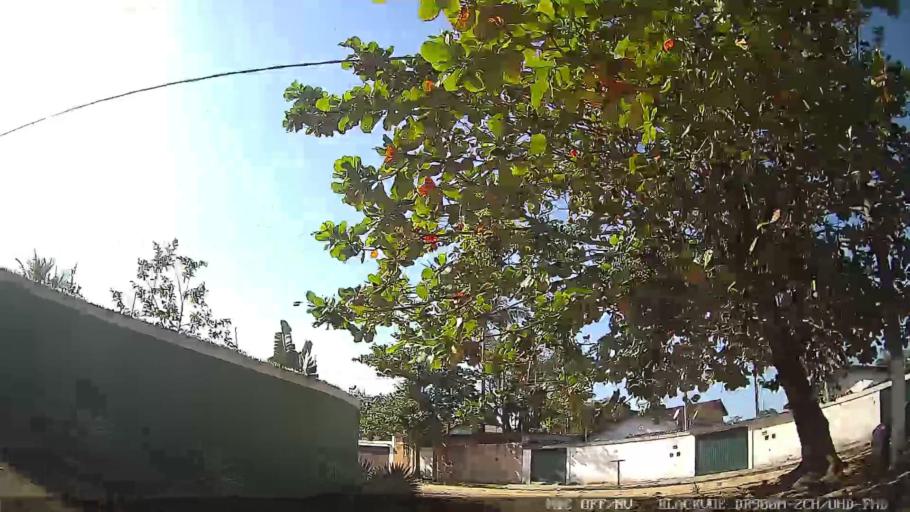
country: BR
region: Sao Paulo
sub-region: Guaruja
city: Guaruja
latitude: -23.9744
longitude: -46.2120
